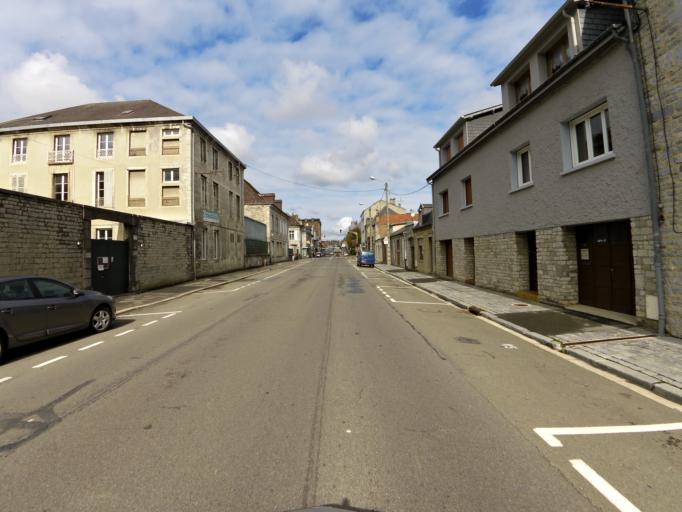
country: FR
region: Champagne-Ardenne
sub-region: Departement des Ardennes
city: Givet
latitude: 50.1341
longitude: 4.8303
